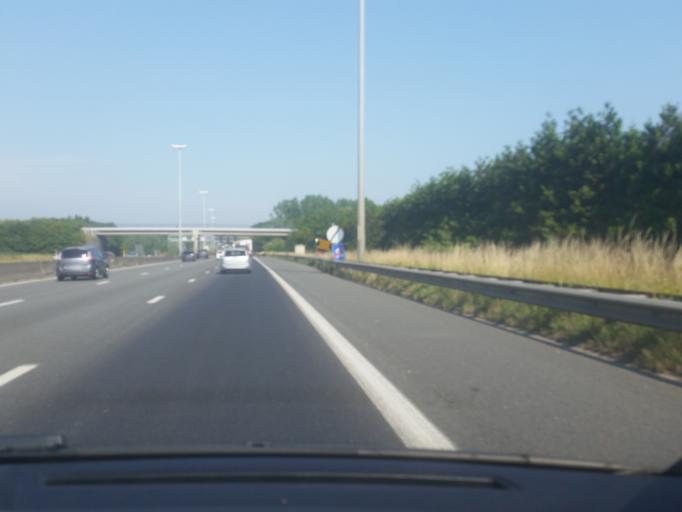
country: BE
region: Flanders
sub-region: Provincie Oost-Vlaanderen
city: Melle
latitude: 50.9849
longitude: 3.8132
